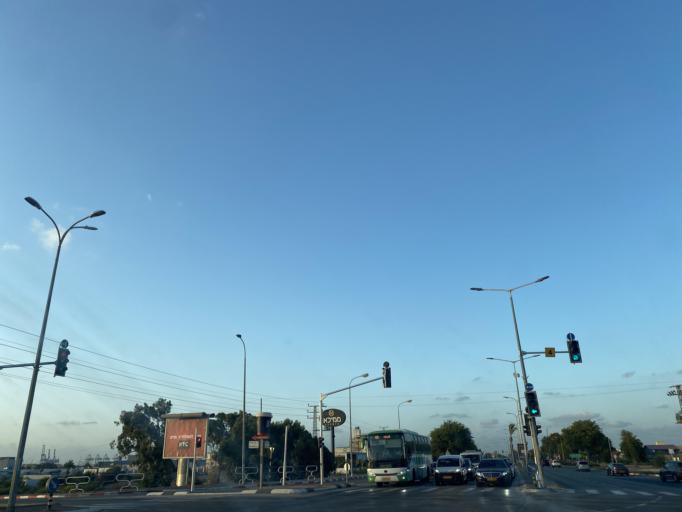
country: IL
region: Southern District
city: Ashdod
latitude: 31.8072
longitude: 34.6632
